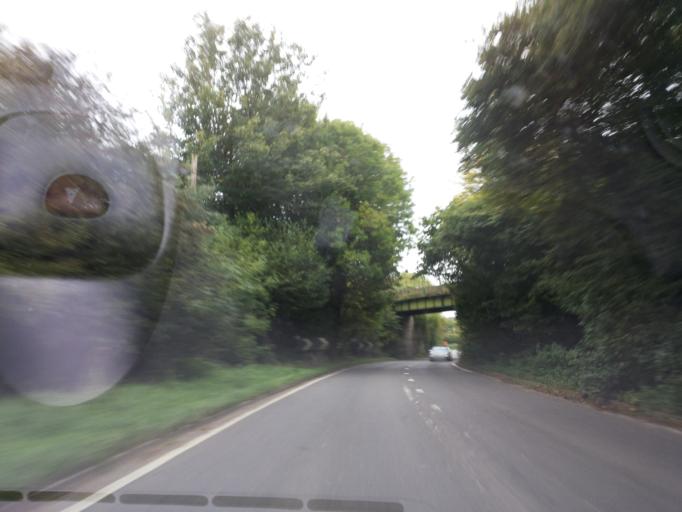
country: GB
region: England
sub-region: Buckinghamshire
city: Great Missenden
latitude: 51.6876
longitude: -0.6878
